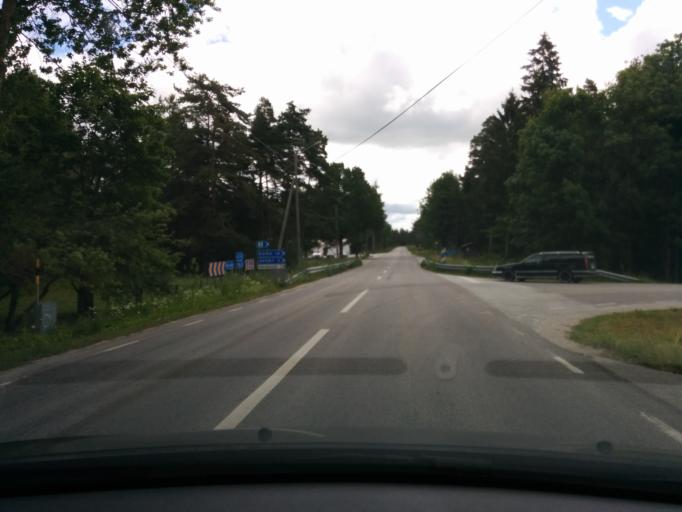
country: SE
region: Gotland
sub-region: Gotland
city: Visby
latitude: 57.6339
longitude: 18.5391
